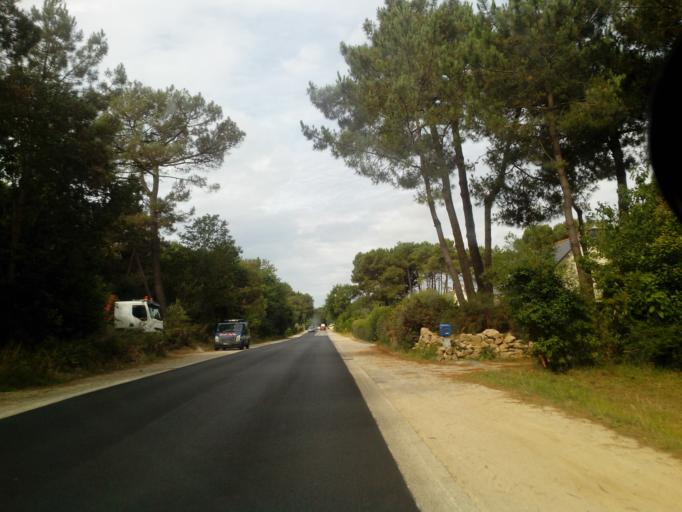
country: FR
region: Brittany
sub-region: Departement du Morbihan
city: Ploemel
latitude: 47.6439
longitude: -3.0905
